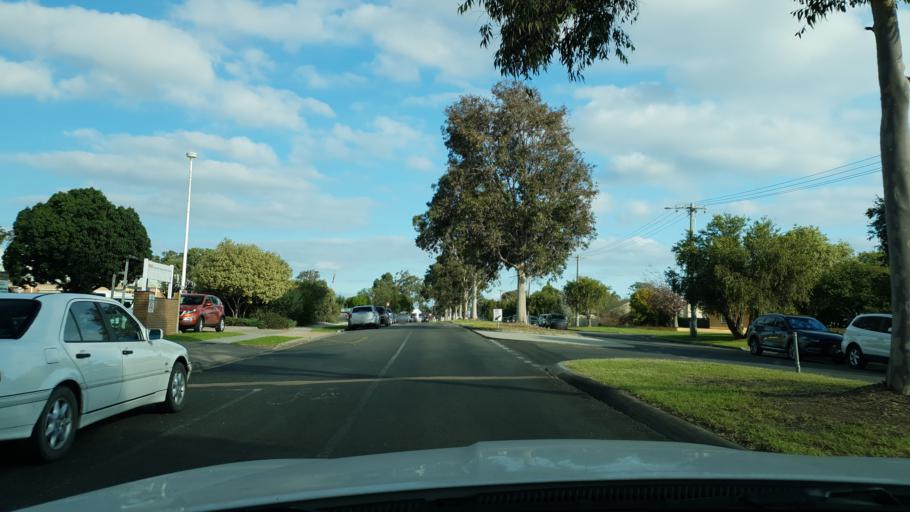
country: AU
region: Victoria
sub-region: East Gippsland
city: Bairnsdale
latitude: -37.8311
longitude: 147.6062
